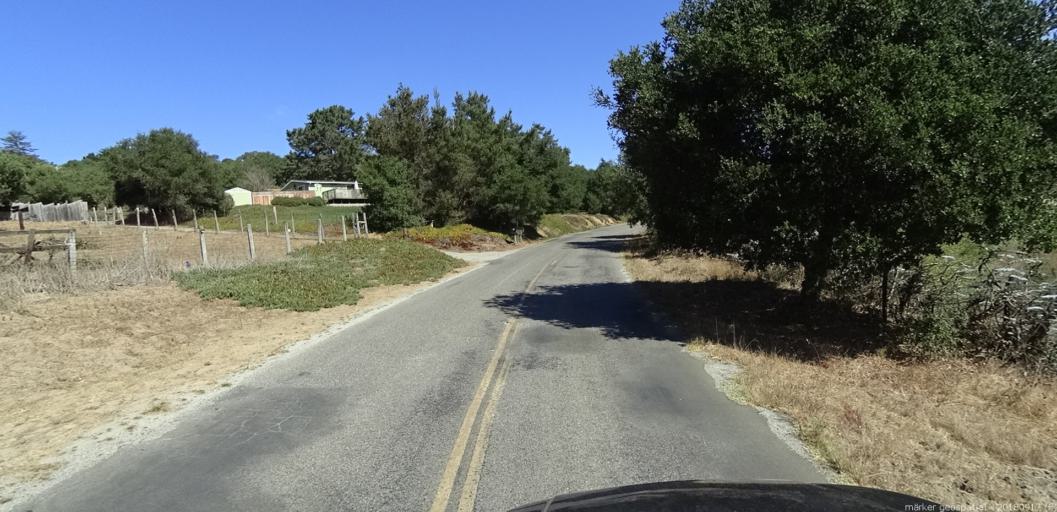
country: US
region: California
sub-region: Monterey County
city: Elkhorn
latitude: 36.8326
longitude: -121.7262
